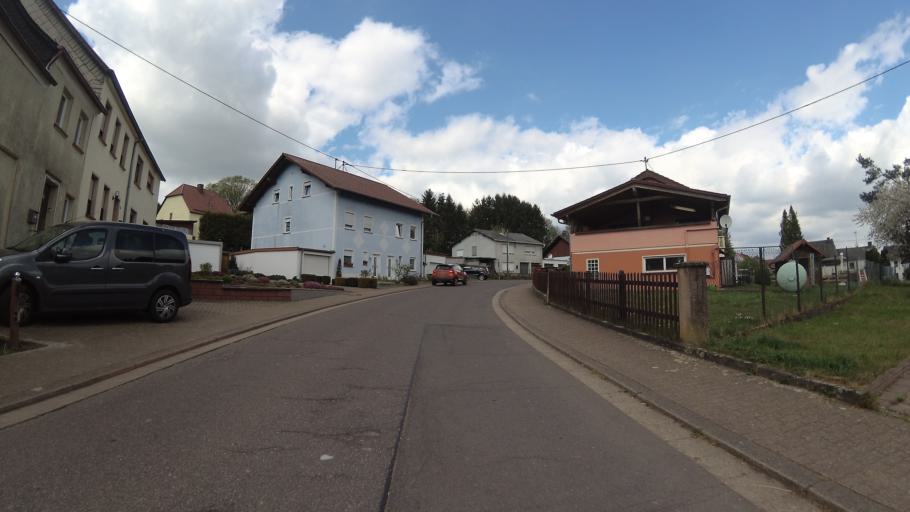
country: DE
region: Saarland
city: Wadern
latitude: 49.5234
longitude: 6.8627
